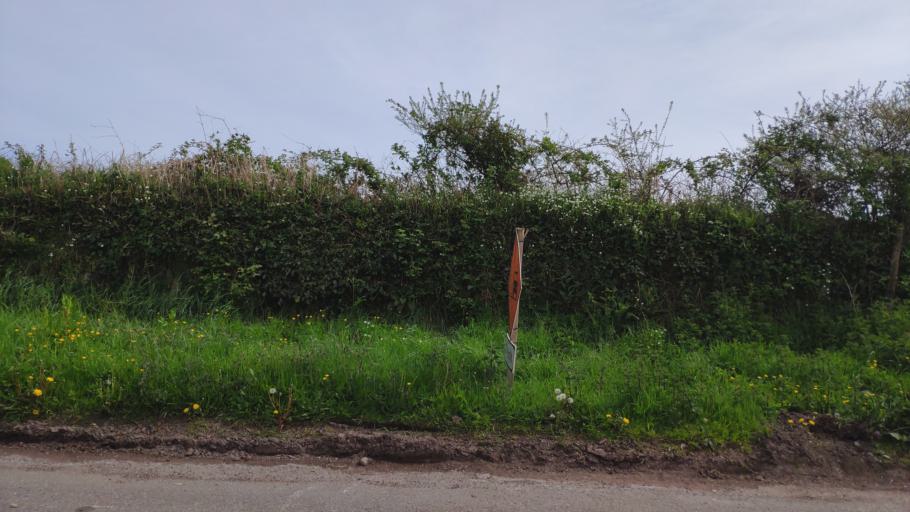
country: IE
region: Munster
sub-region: County Cork
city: Blarney
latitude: 51.9585
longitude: -8.5109
